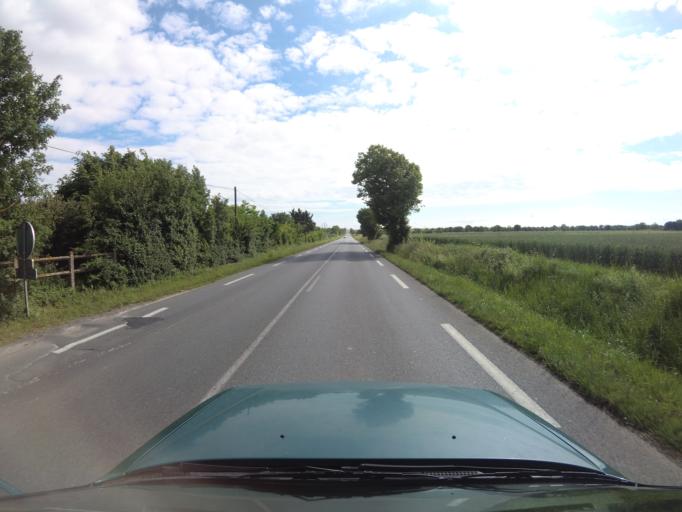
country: FR
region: Poitou-Charentes
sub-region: Departement de la Charente-Maritime
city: Saint-Xandre
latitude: 46.2324
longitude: -1.0759
